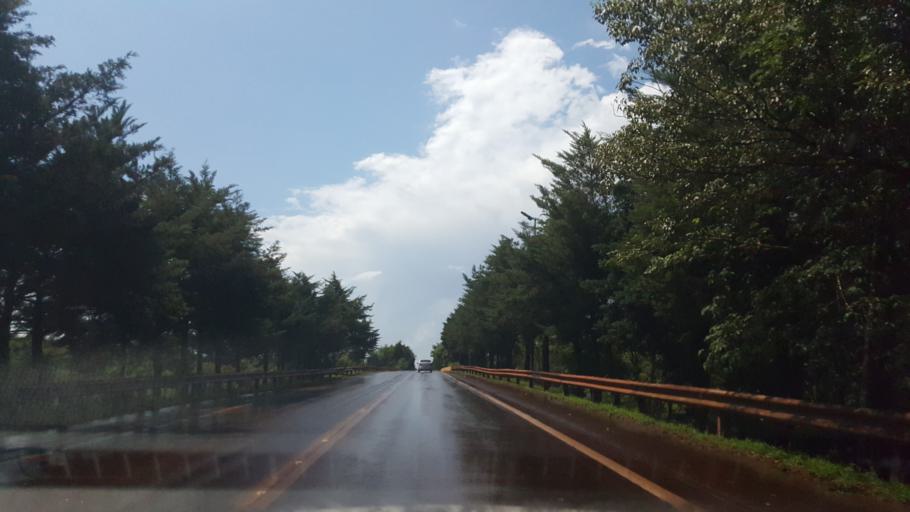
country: AR
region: Misiones
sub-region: Departamento de Eldorado
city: Eldorado
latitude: -26.4045
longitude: -54.6353
